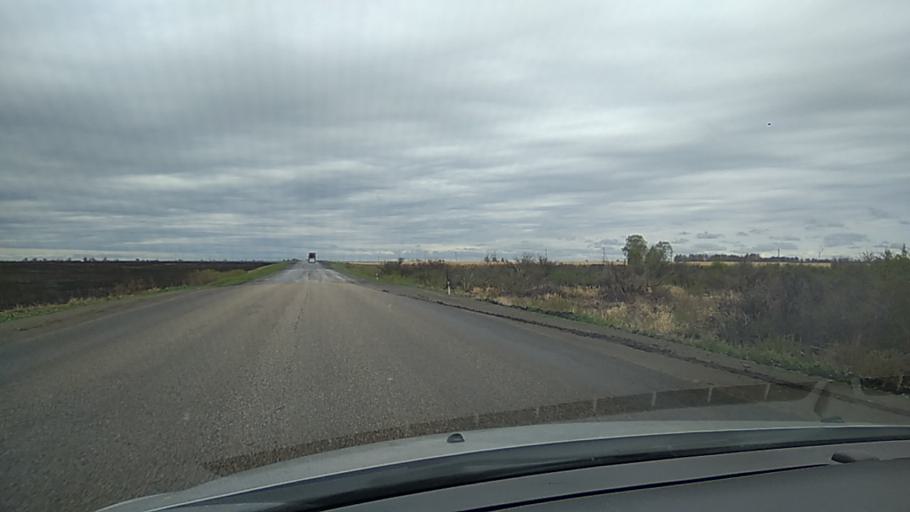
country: RU
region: Kurgan
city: Shatrovo
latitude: 56.4055
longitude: 64.9516
